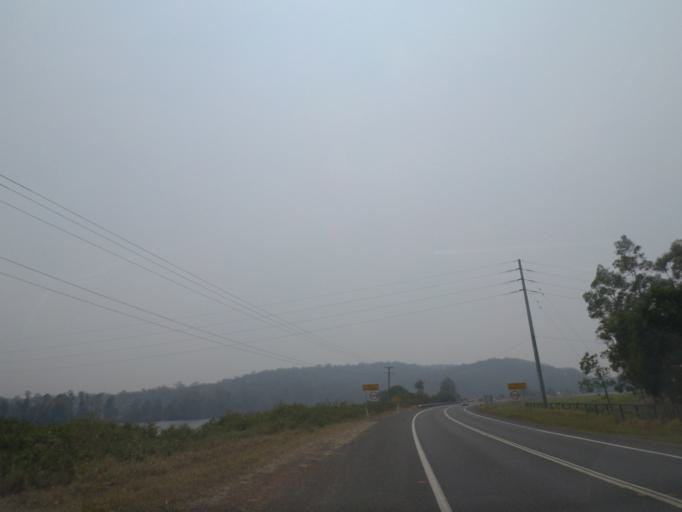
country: AU
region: New South Wales
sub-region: Clarence Valley
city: Maclean
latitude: -29.5434
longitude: 153.1564
